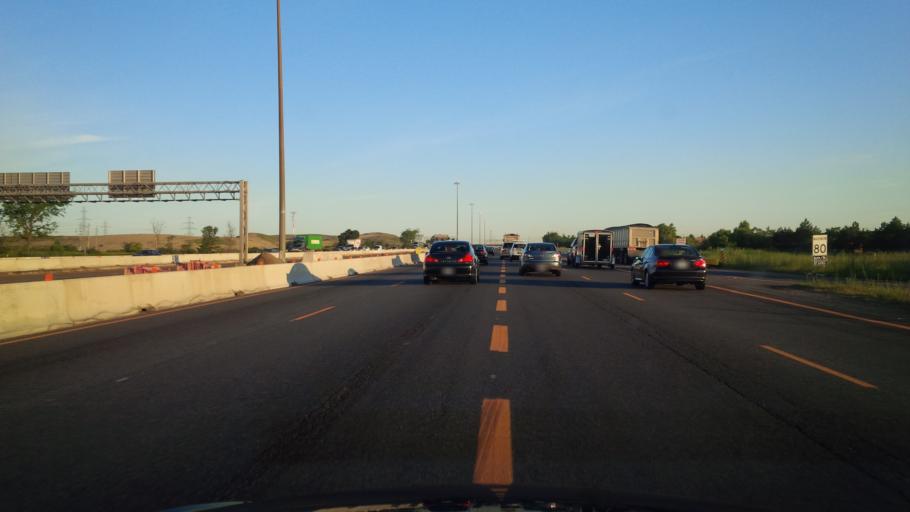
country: CA
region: Ontario
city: Mississauga
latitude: 43.6439
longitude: -79.6664
